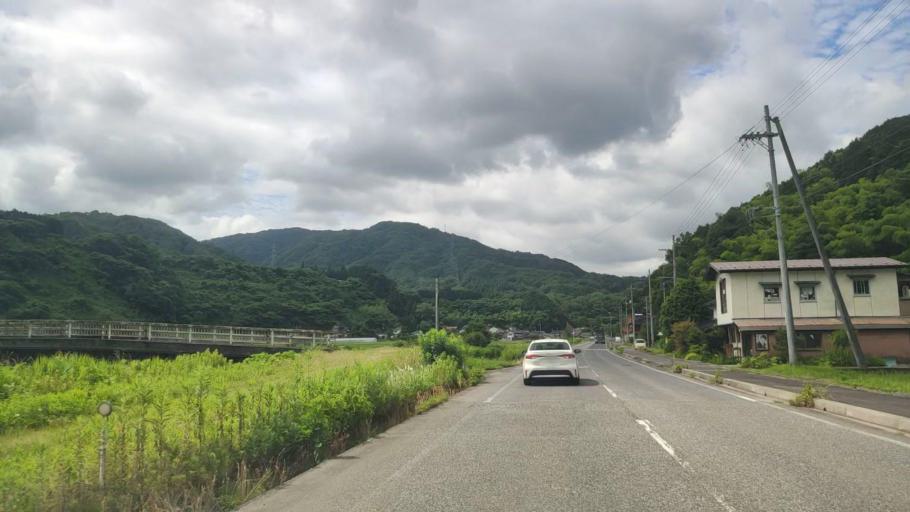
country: JP
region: Tottori
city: Yonago
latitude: 35.3249
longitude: 133.4307
